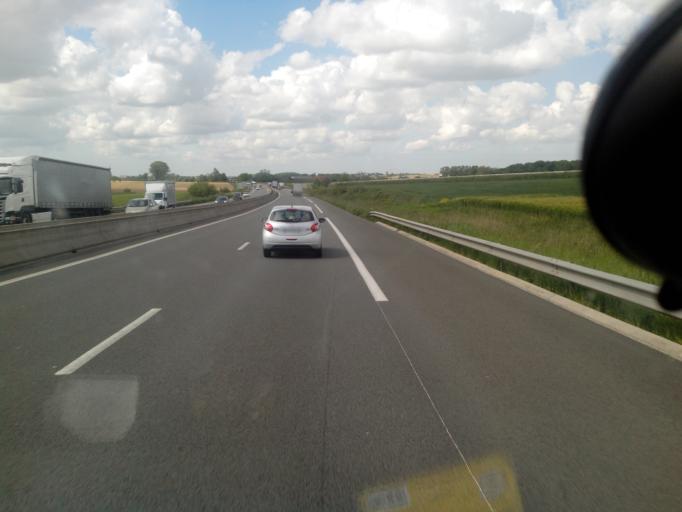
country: FR
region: Nord-Pas-de-Calais
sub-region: Departement du Nord
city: Godewaersvelde
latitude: 50.7893
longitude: 2.6202
